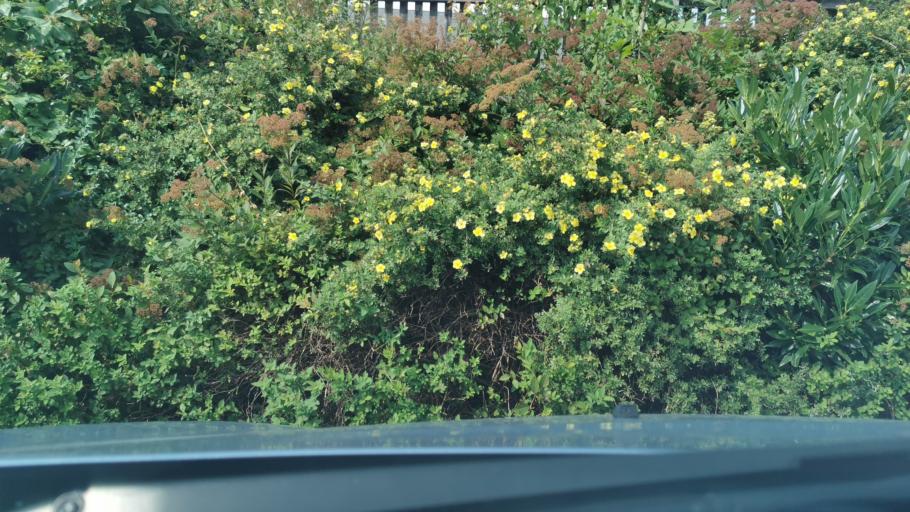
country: AT
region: Styria
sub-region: Politischer Bezirk Weiz
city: Strallegg
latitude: 47.3940
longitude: 15.6838
